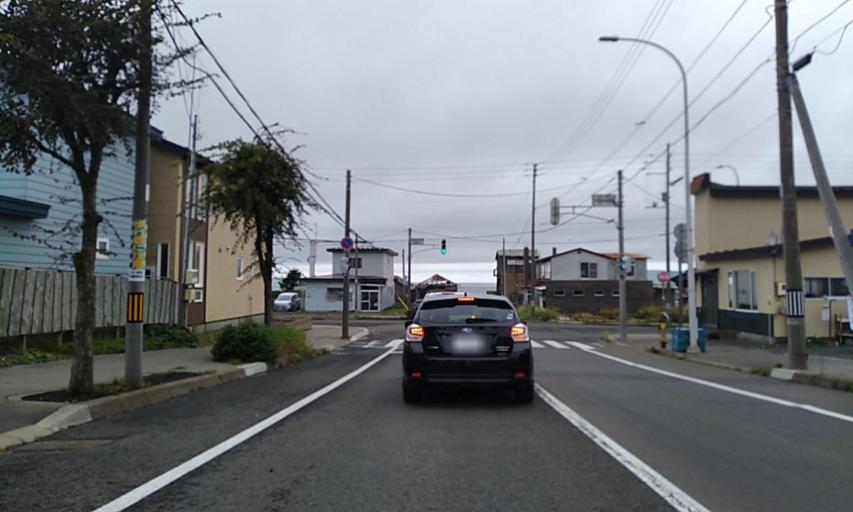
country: JP
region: Hokkaido
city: Nemuro
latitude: 43.3303
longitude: 145.5738
